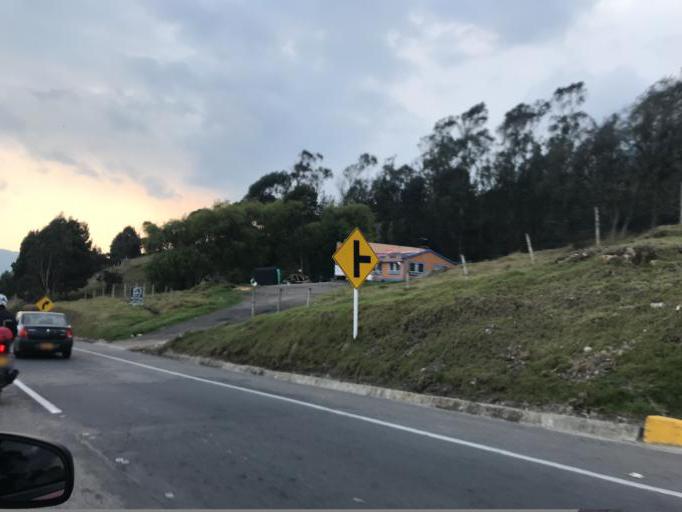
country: CO
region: Boyaca
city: Ventaquemada
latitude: 5.3893
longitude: -73.4993
